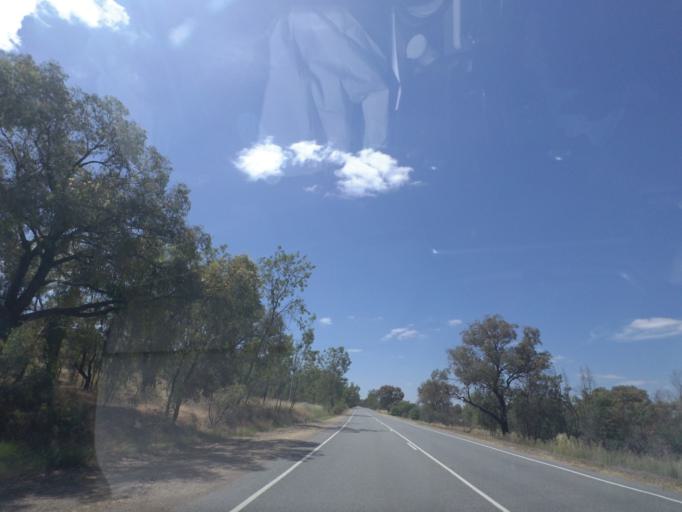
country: AU
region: Victoria
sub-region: Wangaratta
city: Wangaratta
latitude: -36.4567
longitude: 146.2366
